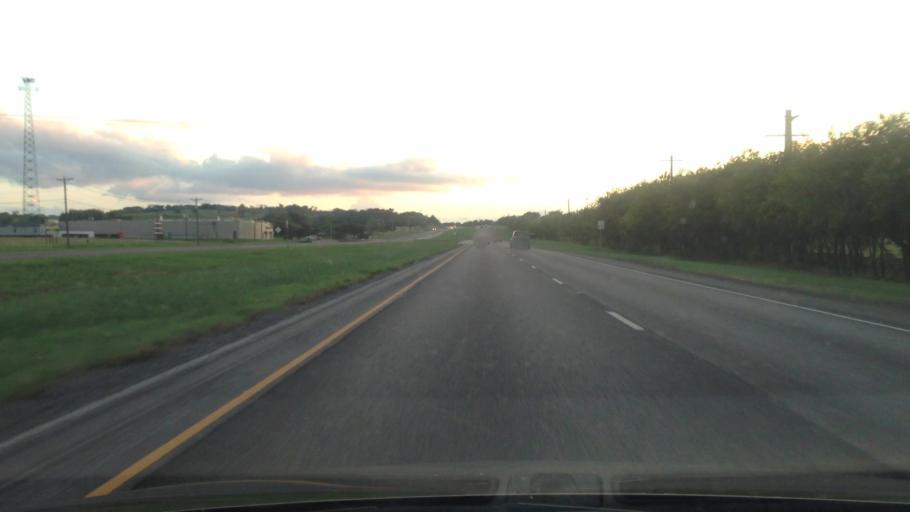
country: US
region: Texas
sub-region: Tarrant County
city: Benbrook
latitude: 32.6154
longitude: -97.5407
